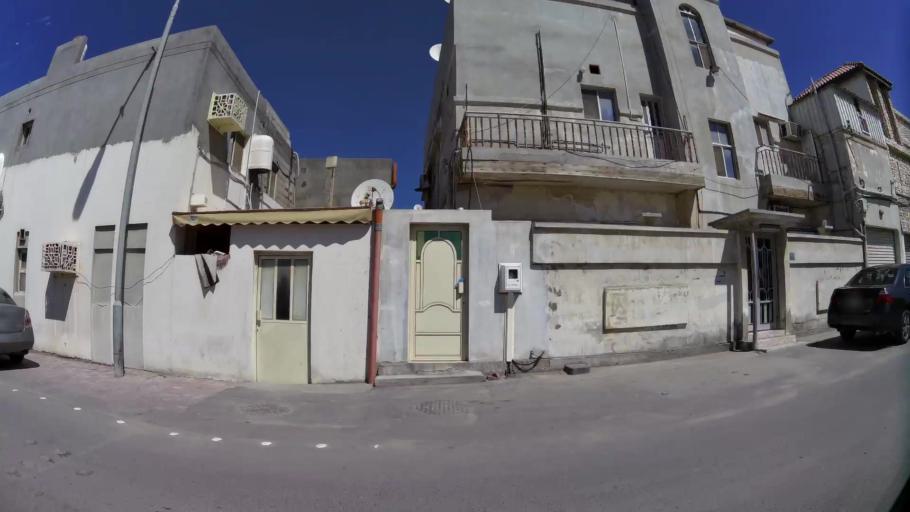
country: BH
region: Muharraq
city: Al Muharraq
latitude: 26.2811
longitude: 50.6329
